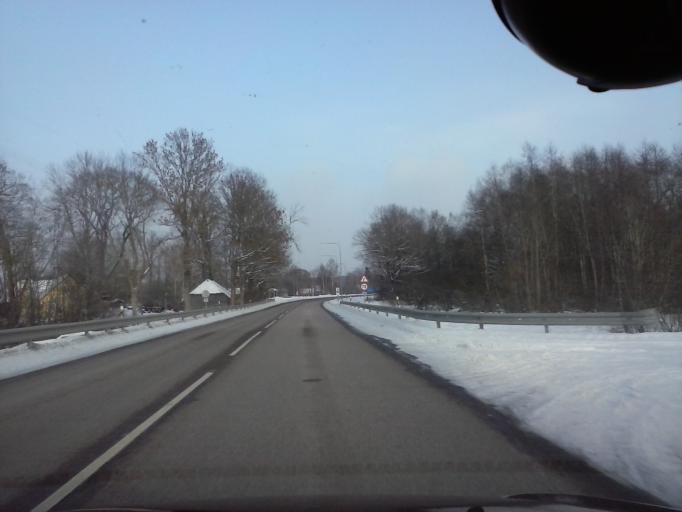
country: EE
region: Jogevamaa
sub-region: Poltsamaa linn
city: Poltsamaa
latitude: 58.4186
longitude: 26.0299
